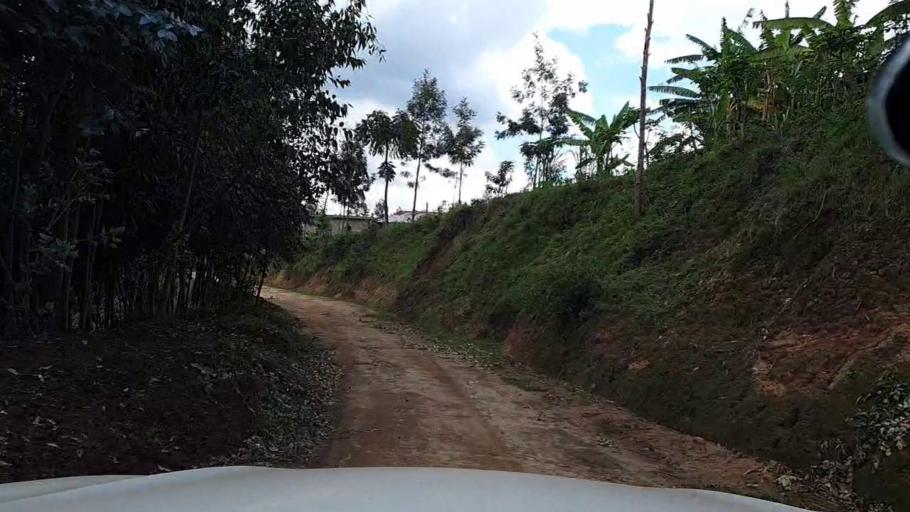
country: RW
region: Southern Province
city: Nzega
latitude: -2.6364
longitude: 29.4856
